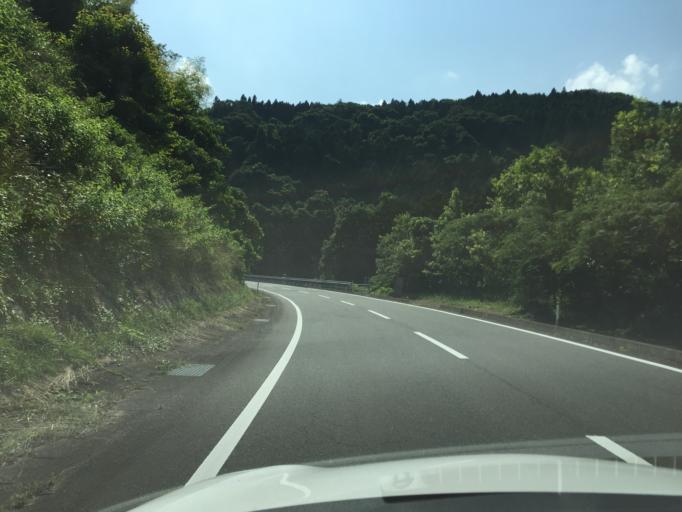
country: JP
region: Ibaraki
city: Kitaibaraki
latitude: 36.9388
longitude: 140.7292
